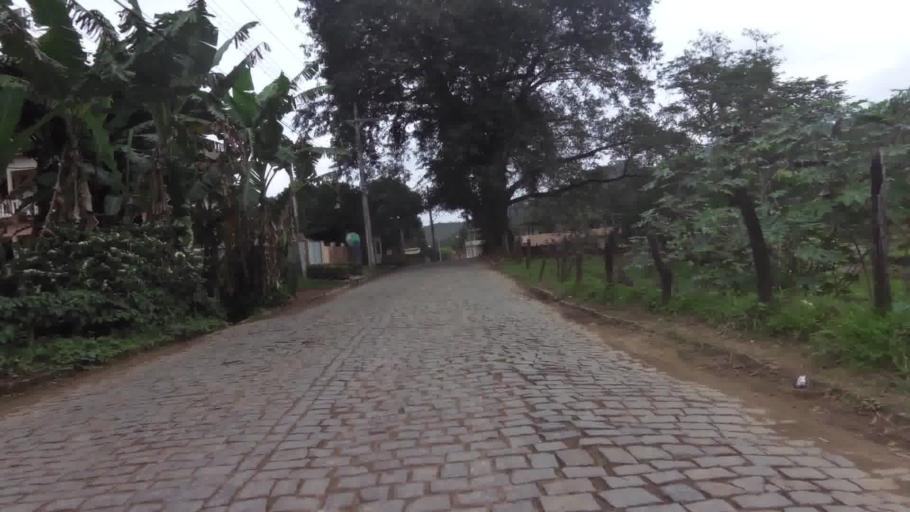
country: BR
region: Espirito Santo
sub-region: Iconha
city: Iconha
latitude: -20.7602
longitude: -40.8359
